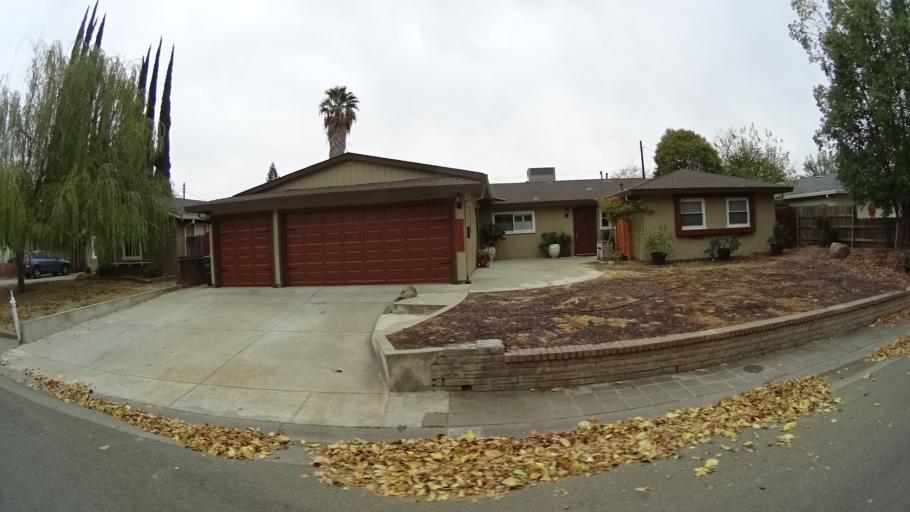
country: US
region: California
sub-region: Sacramento County
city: Antelope
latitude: 38.6988
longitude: -121.3069
